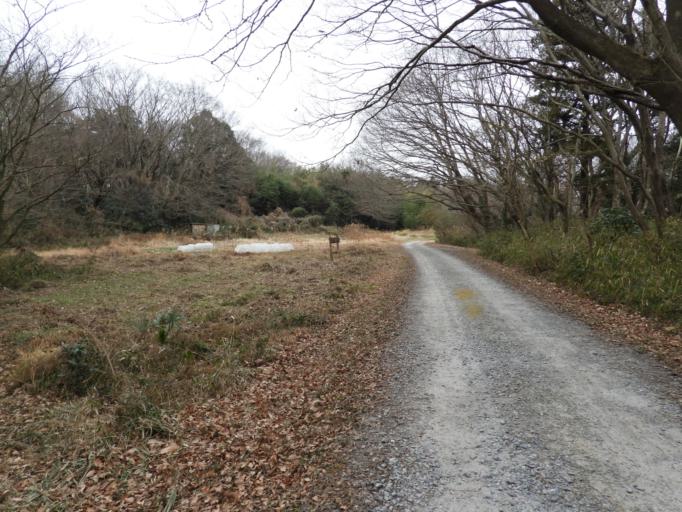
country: JP
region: Ibaraki
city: Naka
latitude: 36.0787
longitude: 140.1656
